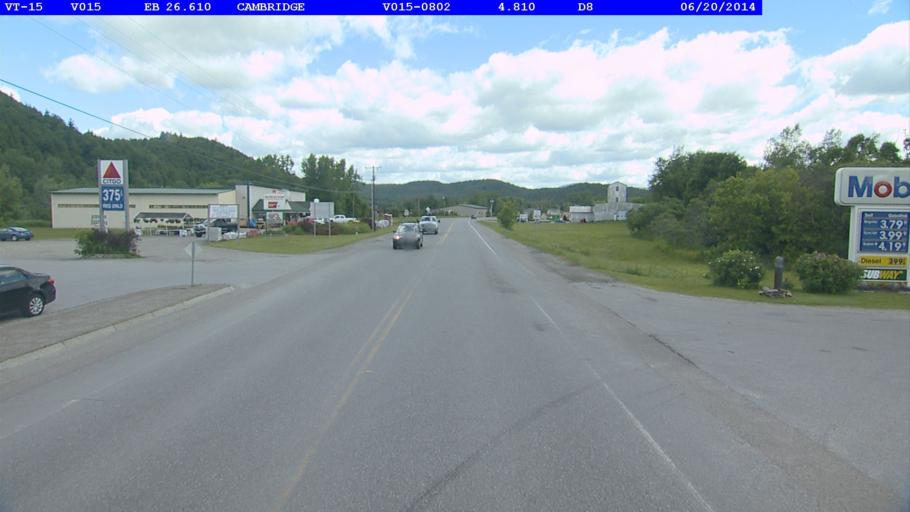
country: US
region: Vermont
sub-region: Lamoille County
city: Johnson
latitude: 44.6447
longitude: -72.8340
